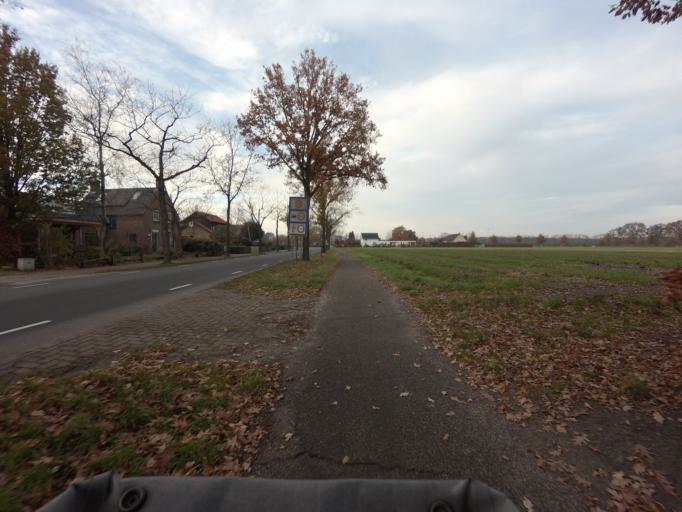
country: NL
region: North Brabant
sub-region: Gemeente Breda
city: Breda
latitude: 51.5015
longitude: 4.7968
